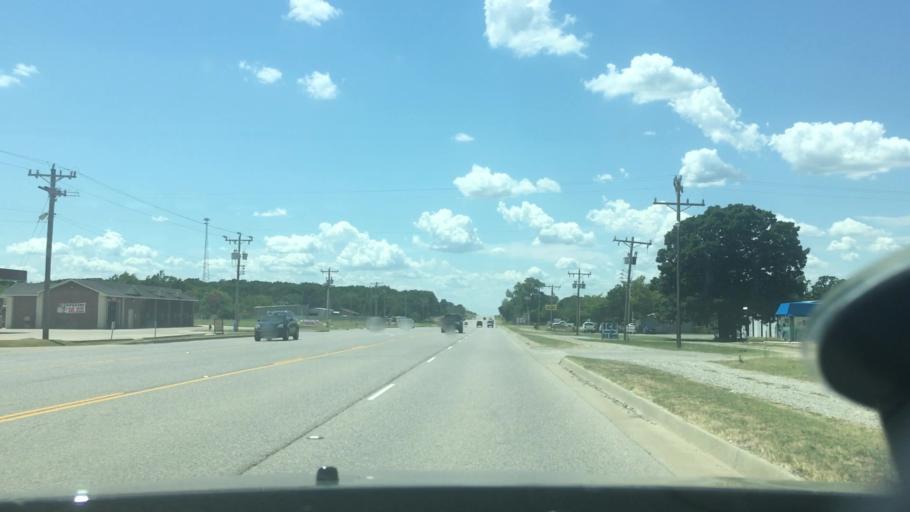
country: US
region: Oklahoma
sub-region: Bryan County
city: Calera
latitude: 33.9983
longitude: -96.5267
